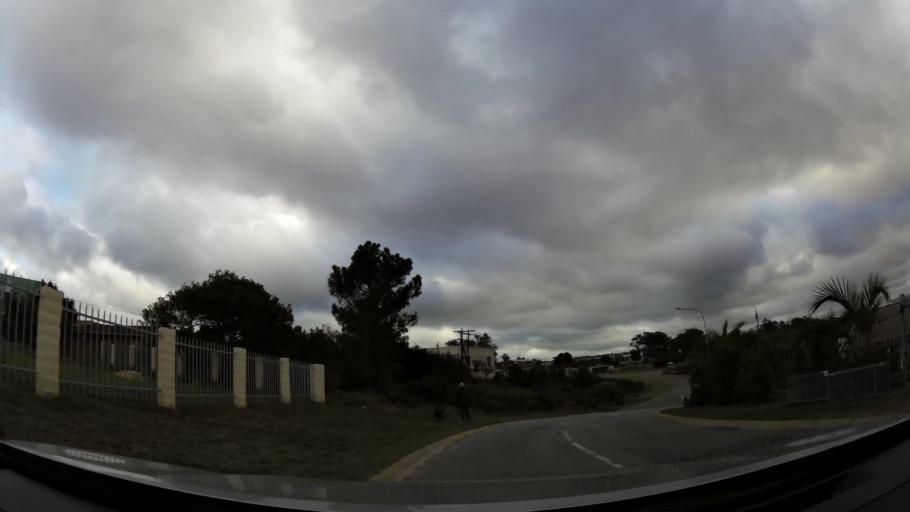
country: ZA
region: Western Cape
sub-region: Eden District Municipality
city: Plettenberg Bay
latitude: -34.0486
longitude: 23.3626
